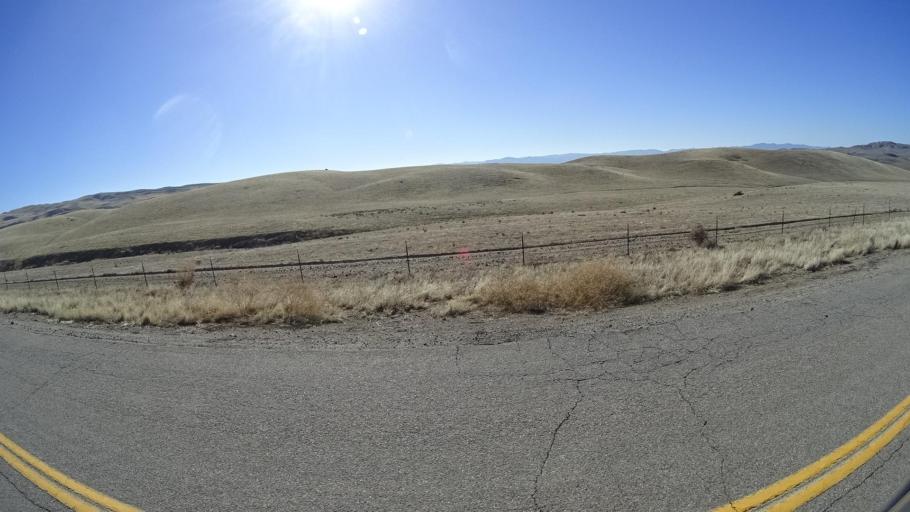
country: US
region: California
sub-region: Kern County
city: Maricopa
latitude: 34.9551
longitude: -119.4342
